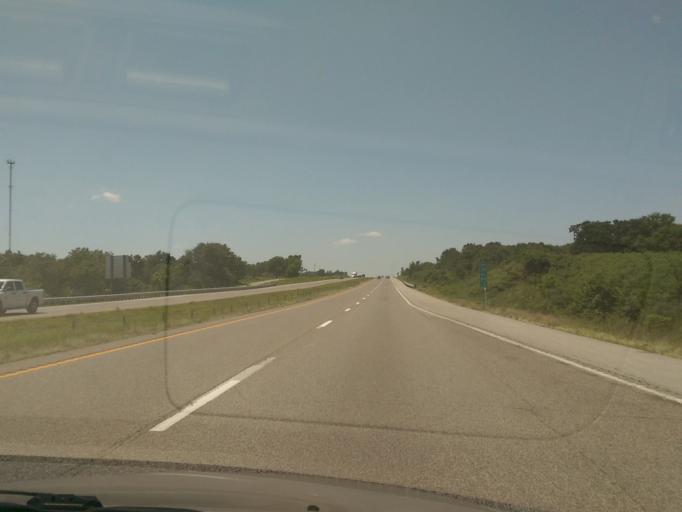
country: US
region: Missouri
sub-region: Saline County
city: Marshall
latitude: 38.9535
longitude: -93.0926
